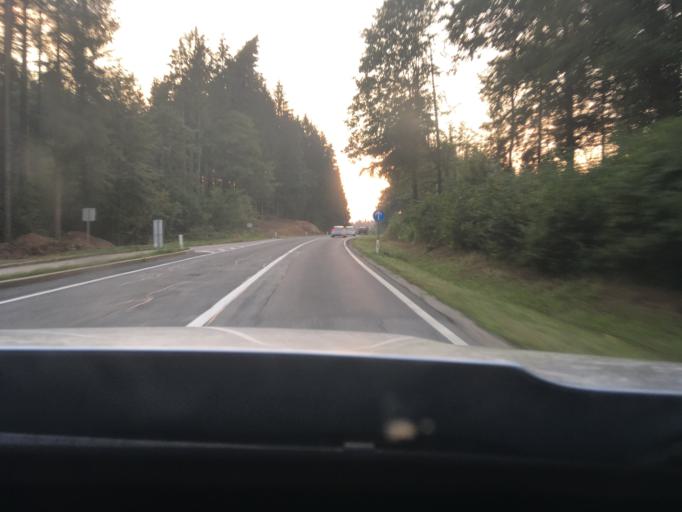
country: SI
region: Kocevje
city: Kocevje
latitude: 45.6822
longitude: 14.8194
